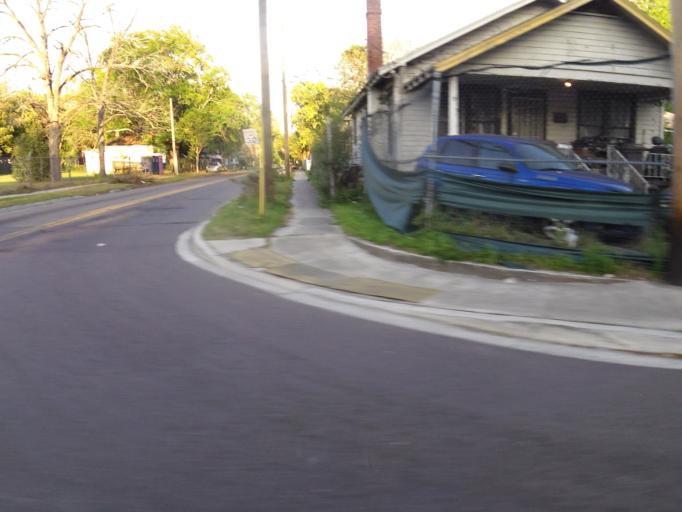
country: US
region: Florida
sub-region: Duval County
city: Jacksonville
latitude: 30.3257
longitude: -81.7054
